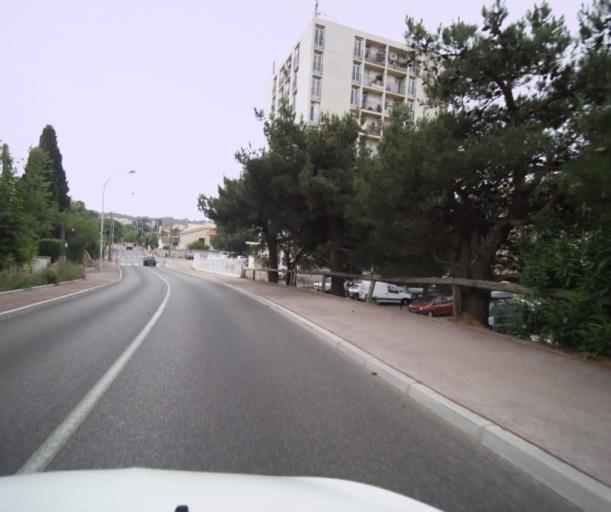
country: FR
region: Provence-Alpes-Cote d'Azur
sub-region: Departement du Var
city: La Valette-du-Var
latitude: 43.1332
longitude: 5.9872
